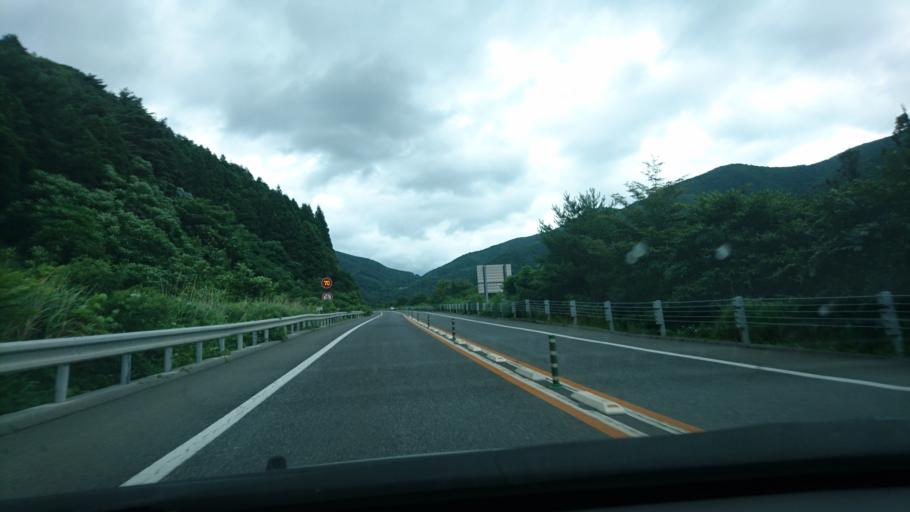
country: JP
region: Iwate
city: Ofunato
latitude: 39.1257
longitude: 141.7448
